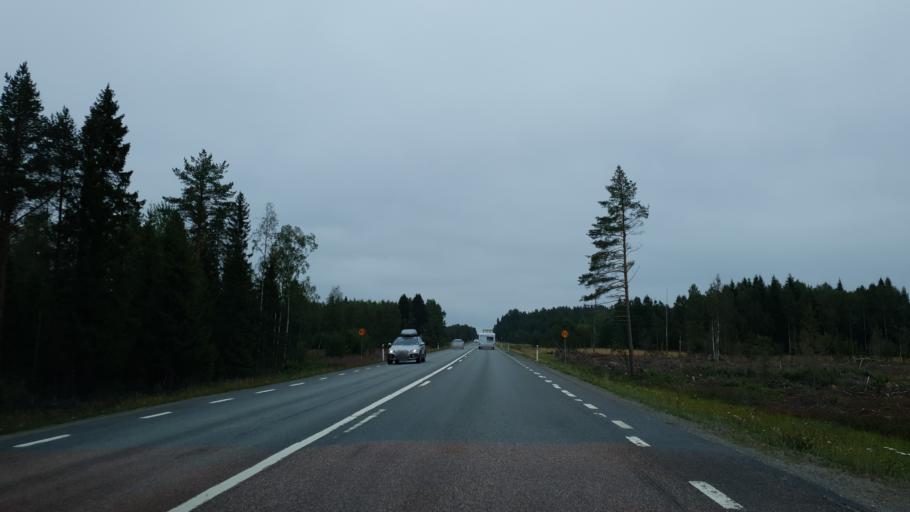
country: SE
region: Vaesterbotten
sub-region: Skelleftea Kommun
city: Burea
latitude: 64.3356
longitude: 21.2700
